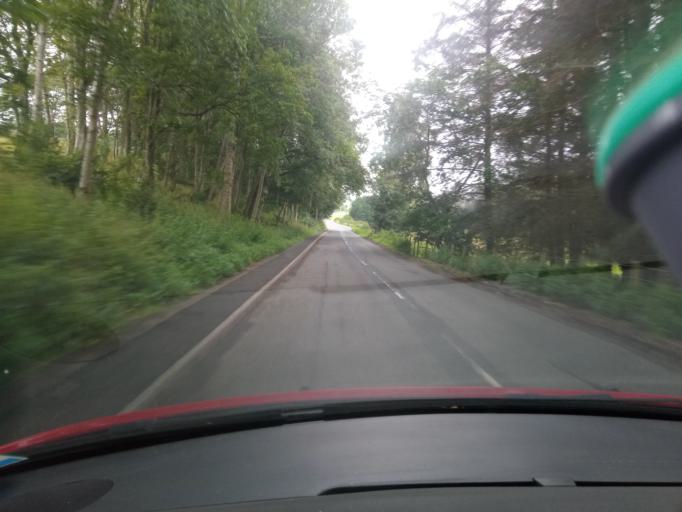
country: GB
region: Scotland
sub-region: Fife
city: Pathhead
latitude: 55.7360
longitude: -2.9123
